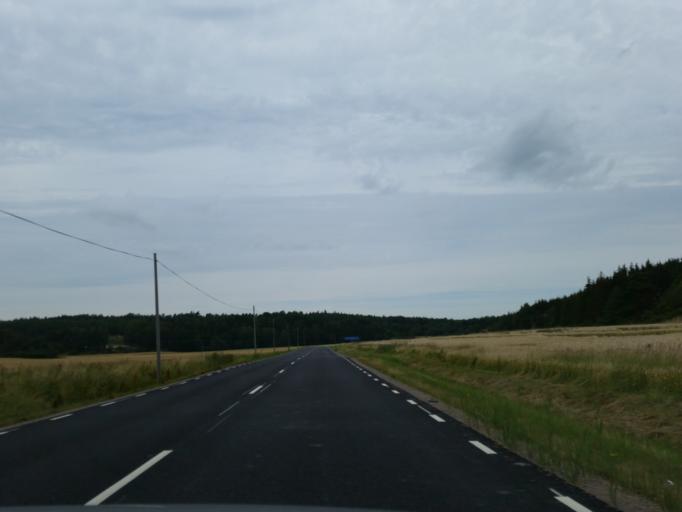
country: SE
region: Soedermanland
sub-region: Strangnas Kommun
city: Mariefred
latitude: 59.2556
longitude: 17.1792
